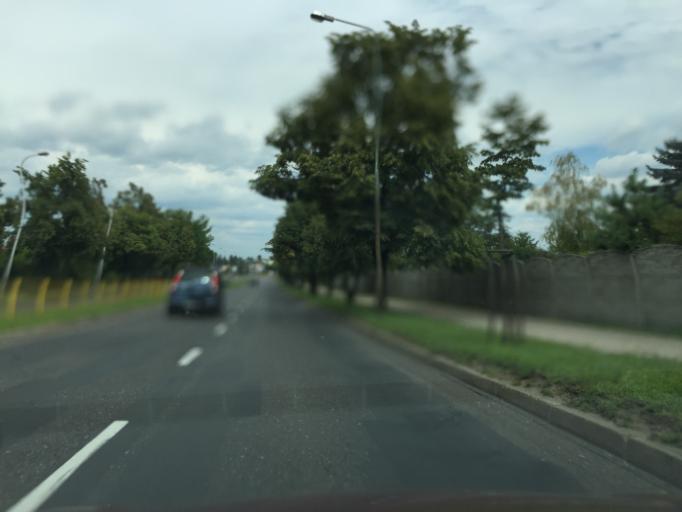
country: PL
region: Greater Poland Voivodeship
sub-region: Kalisz
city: Kalisz
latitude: 51.7524
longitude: 18.0701
